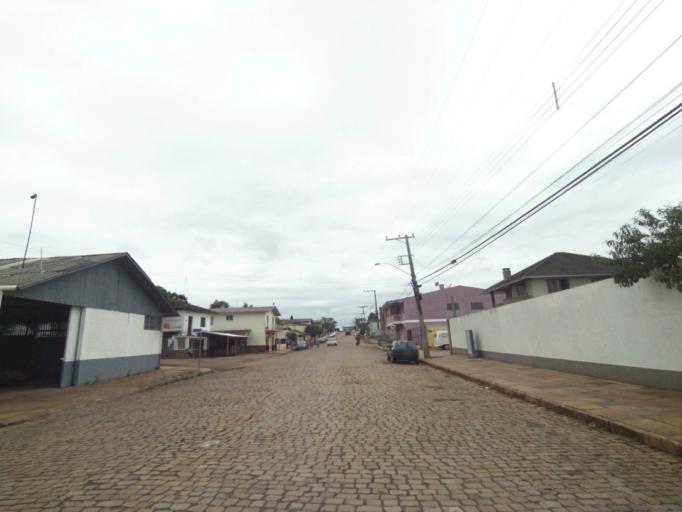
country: BR
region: Rio Grande do Sul
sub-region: Lagoa Vermelha
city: Lagoa Vermelha
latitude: -28.2149
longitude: -51.5339
